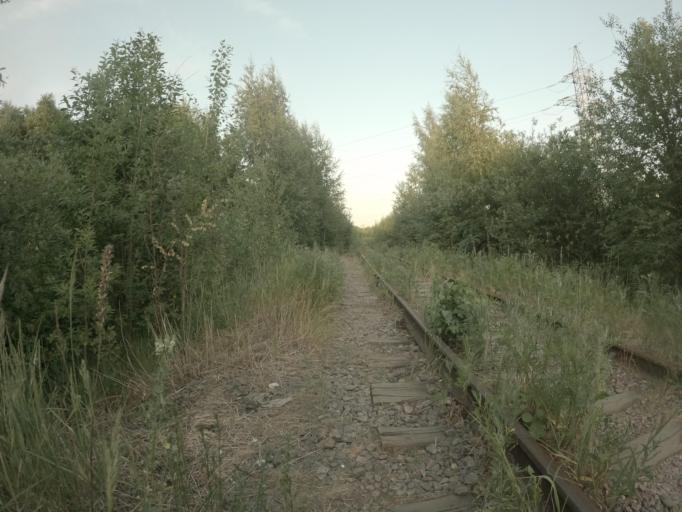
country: RU
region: St.-Petersburg
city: Krasnogvargeisky
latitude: 59.9399
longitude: 30.4446
